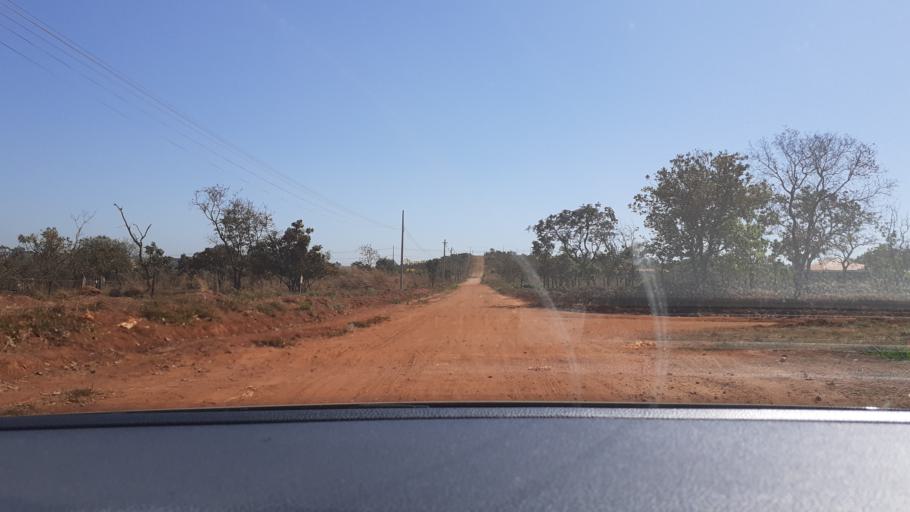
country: BR
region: Goias
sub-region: Aparecida De Goiania
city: Aparecida de Goiania
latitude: -16.8882
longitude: -49.2588
